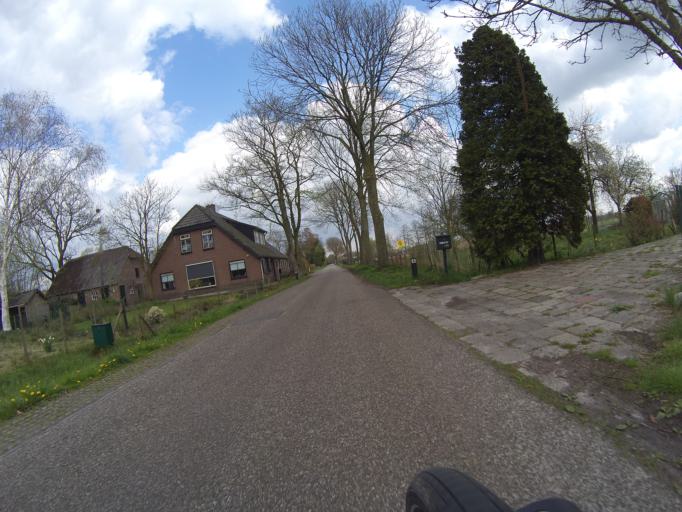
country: NL
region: Gelderland
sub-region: Gemeente Barneveld
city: Zwartebroek
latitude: 52.1826
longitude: 5.4572
